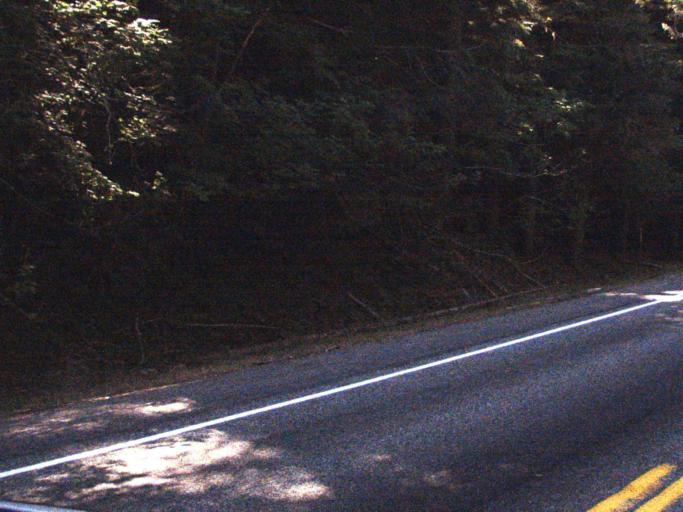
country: US
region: Washington
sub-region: King County
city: Enumclaw
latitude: 47.0405
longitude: -121.5675
